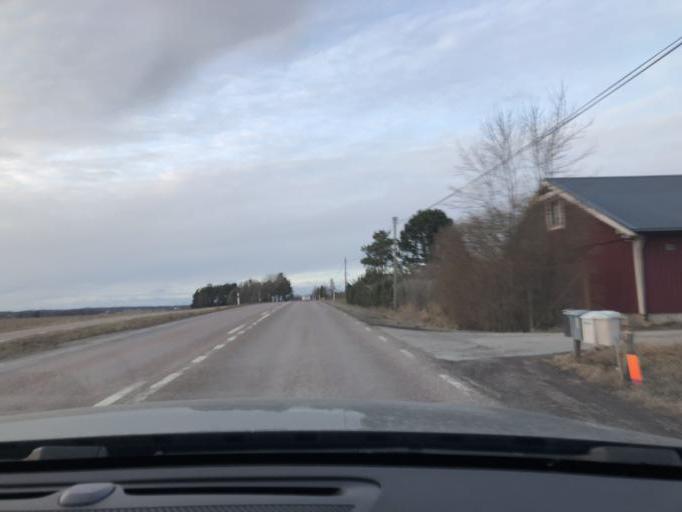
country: SE
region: Uppsala
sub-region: Uppsala Kommun
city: Gamla Uppsala
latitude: 59.9180
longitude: 17.6424
